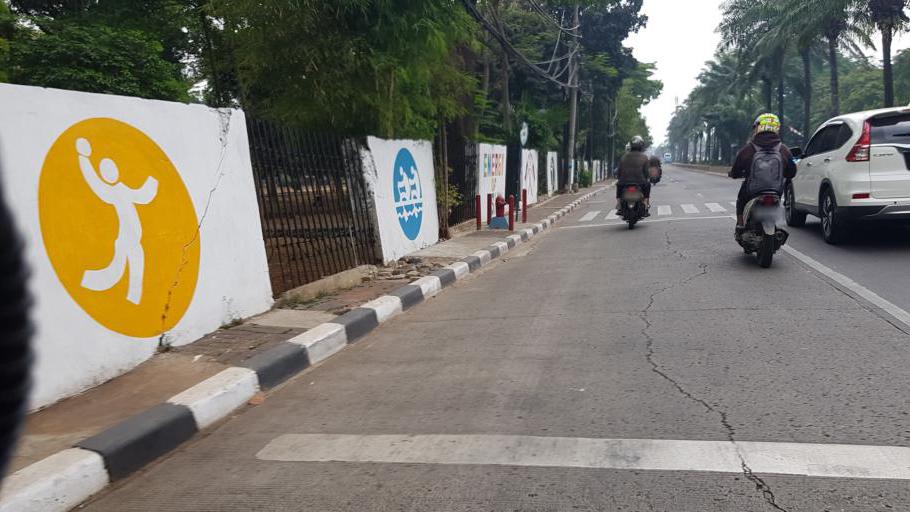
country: ID
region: Jakarta Raya
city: Jakarta
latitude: -6.2972
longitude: 106.8210
